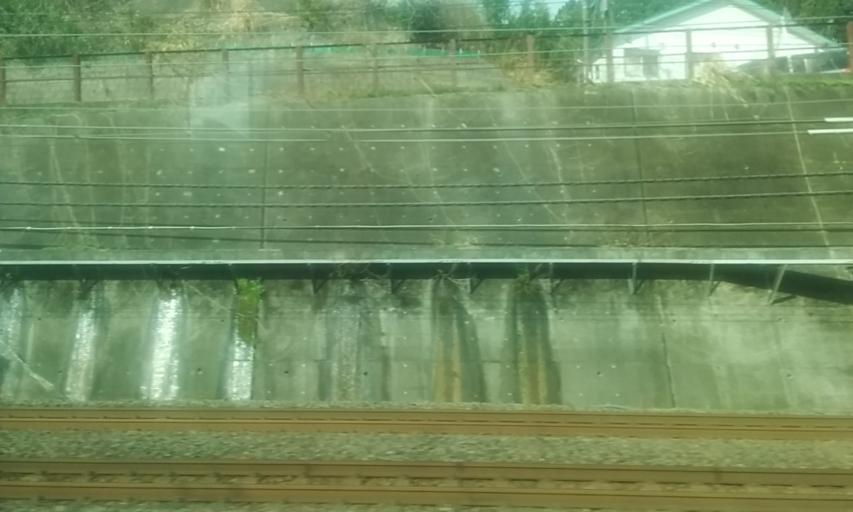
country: JP
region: Kanagawa
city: Yokohama
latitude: 35.4332
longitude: 139.5564
